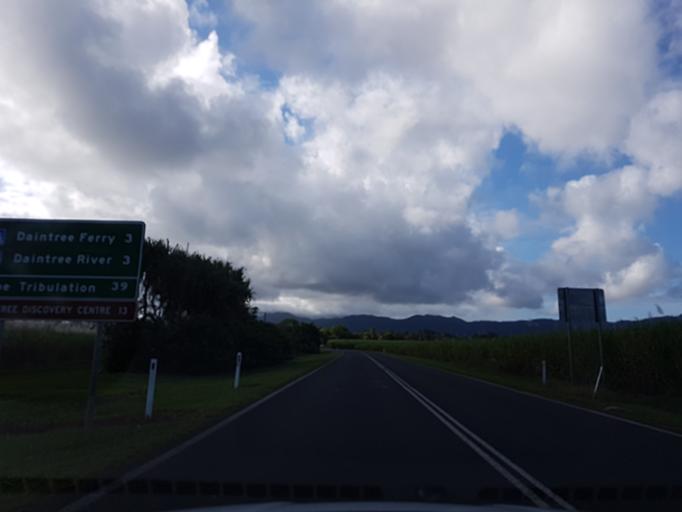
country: AU
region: Queensland
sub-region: Cairns
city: Port Douglas
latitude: -16.2828
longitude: 145.3795
